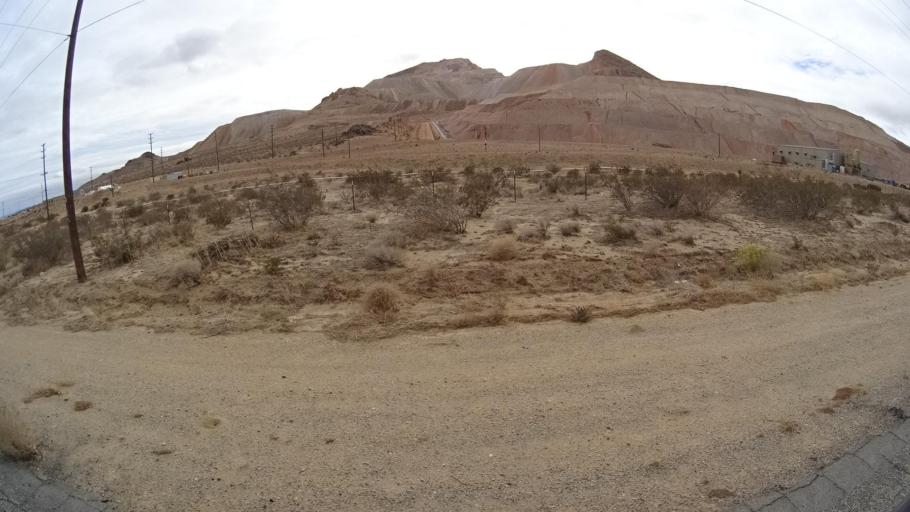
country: US
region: California
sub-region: Kern County
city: Mojave
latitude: 34.9970
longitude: -118.1868
